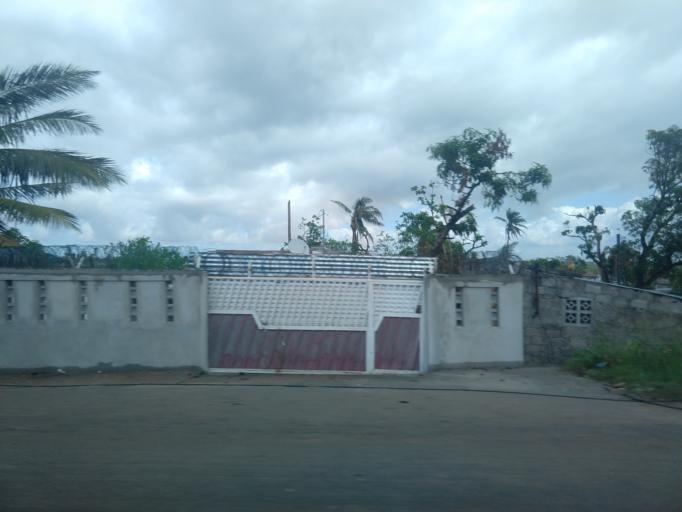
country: MZ
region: Sofala
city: Beira
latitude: -19.7966
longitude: 34.8933
